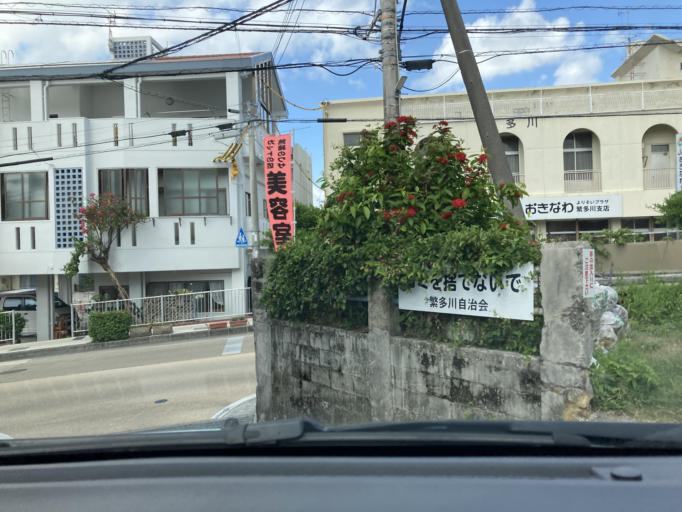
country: JP
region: Okinawa
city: Naha-shi
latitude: 26.2098
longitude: 127.7129
